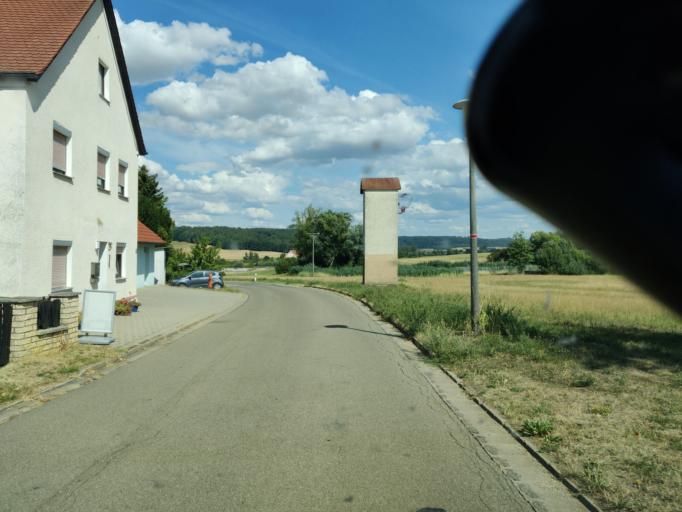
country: DE
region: Bavaria
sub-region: Regierungsbezirk Mittelfranken
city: Thalmassing
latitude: 49.0793
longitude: 11.2426
